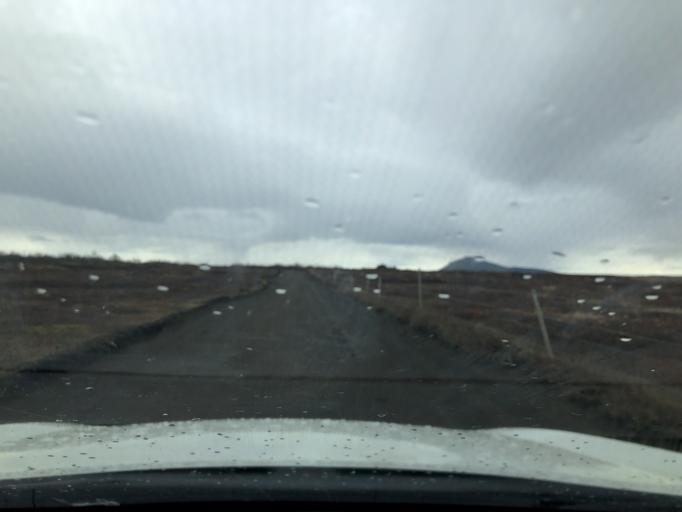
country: IS
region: Northeast
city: Laugar
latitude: 65.6096
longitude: -16.9089
